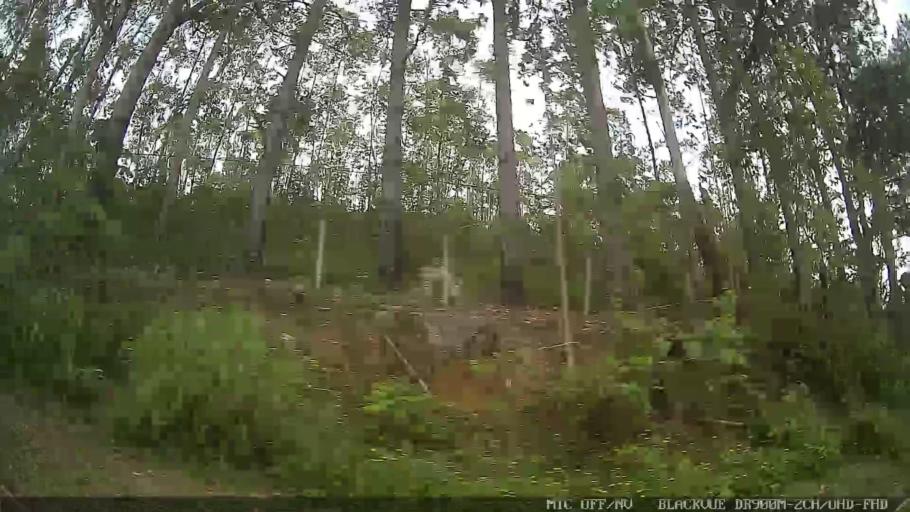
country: BR
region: Sao Paulo
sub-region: Biritiba-Mirim
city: Biritiba Mirim
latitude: -23.5573
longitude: -45.9882
